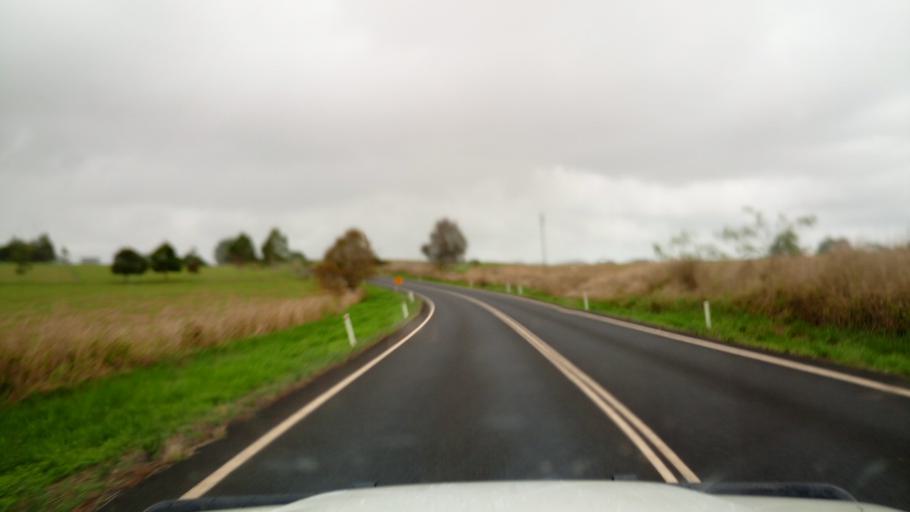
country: AU
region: Queensland
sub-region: Tablelands
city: Atherton
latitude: -17.2807
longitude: 145.6019
